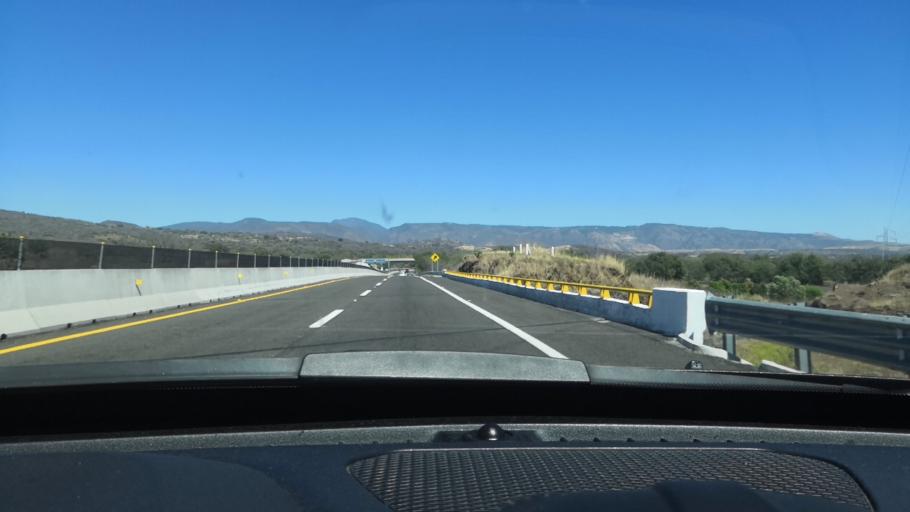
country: MX
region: Nayarit
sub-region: Ahuacatlan
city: Ahuacatlan
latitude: 21.0611
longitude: -104.5074
